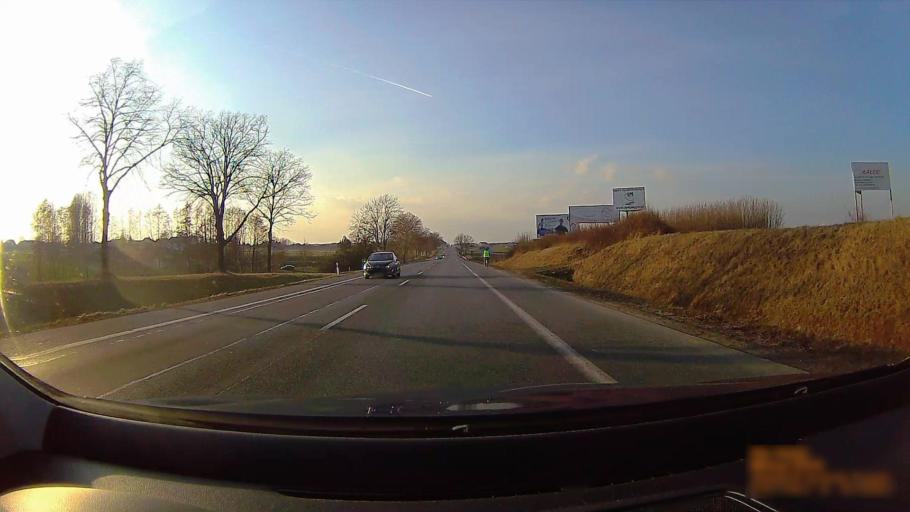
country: PL
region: Greater Poland Voivodeship
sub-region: Konin
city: Konin
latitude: 52.1919
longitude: 18.3268
